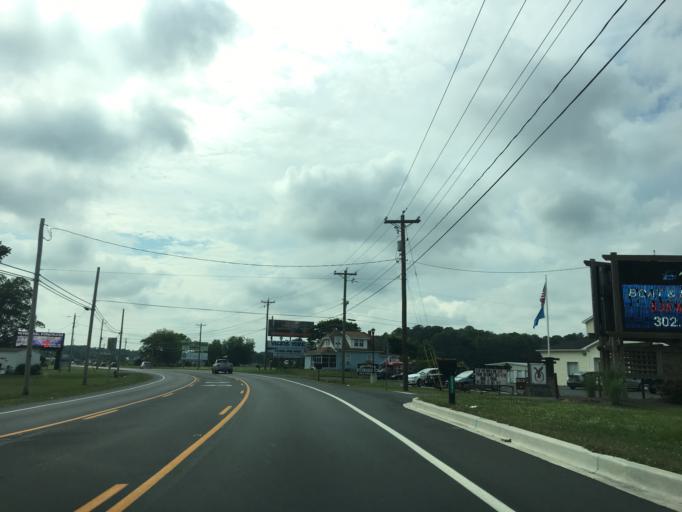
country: US
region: Delaware
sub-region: Sussex County
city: Ocean View
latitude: 38.5509
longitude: -75.1261
